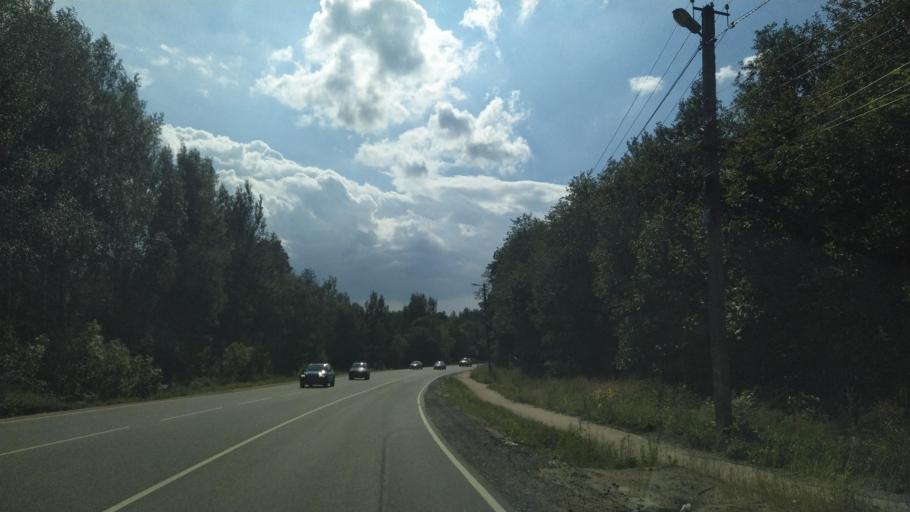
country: RU
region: Leningrad
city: Toksovo
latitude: 60.1563
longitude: 30.5308
